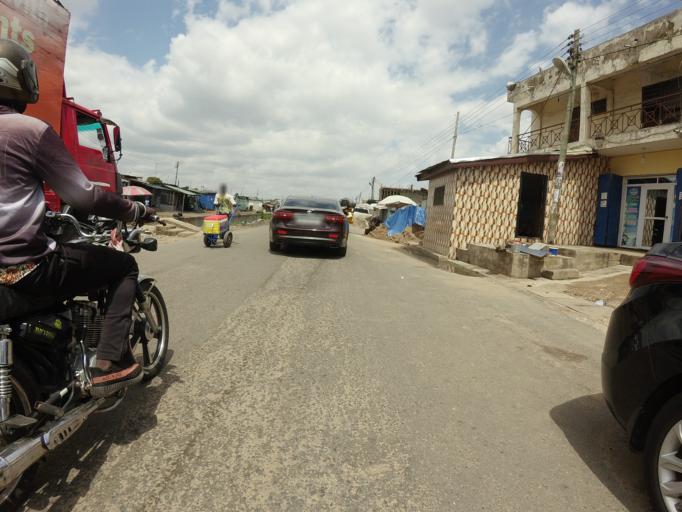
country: GH
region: Greater Accra
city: Accra
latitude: 5.5854
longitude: -0.2018
